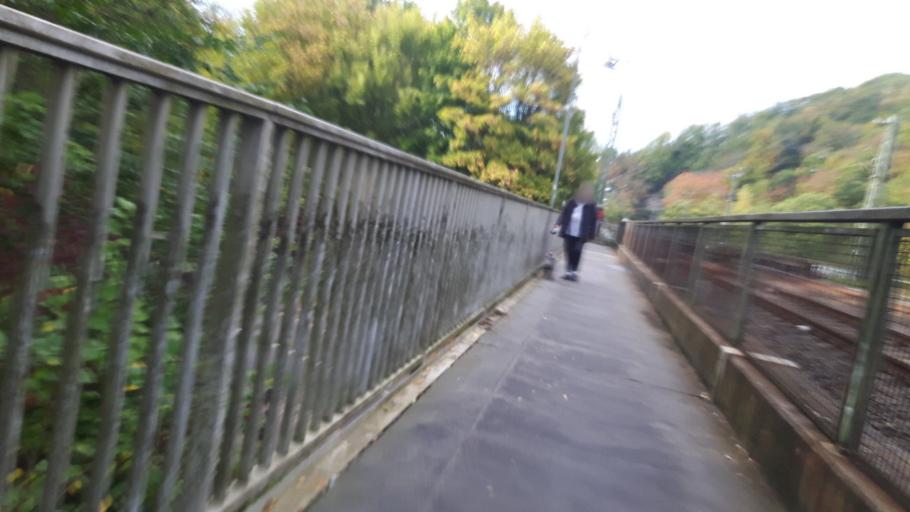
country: DE
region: Rheinland-Pfalz
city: Werkhausen
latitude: 50.7742
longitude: 7.5187
